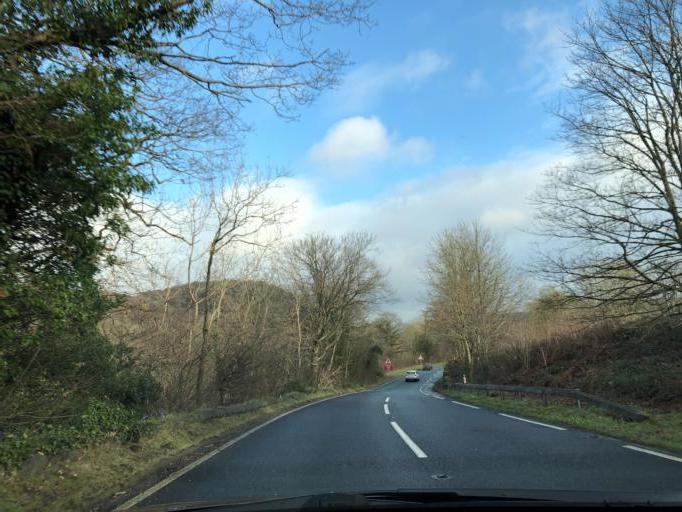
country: GB
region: England
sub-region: Cumbria
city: Grange-over-Sands
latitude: 54.2667
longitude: -2.9782
